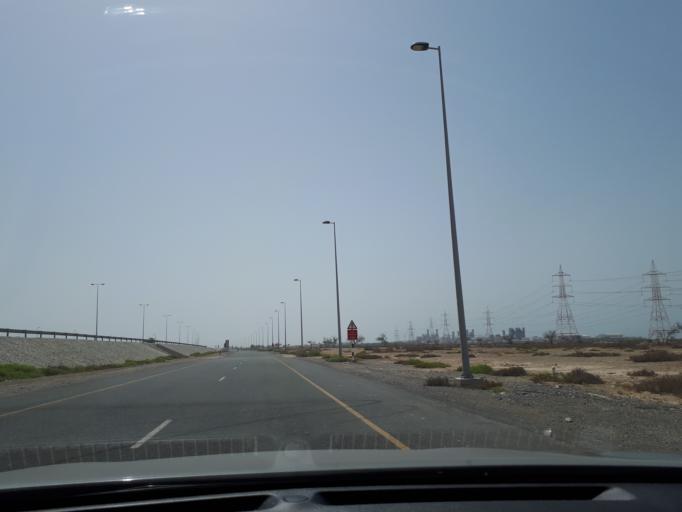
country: OM
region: Al Batinah
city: Barka'
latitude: 23.7006
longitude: 57.9991
